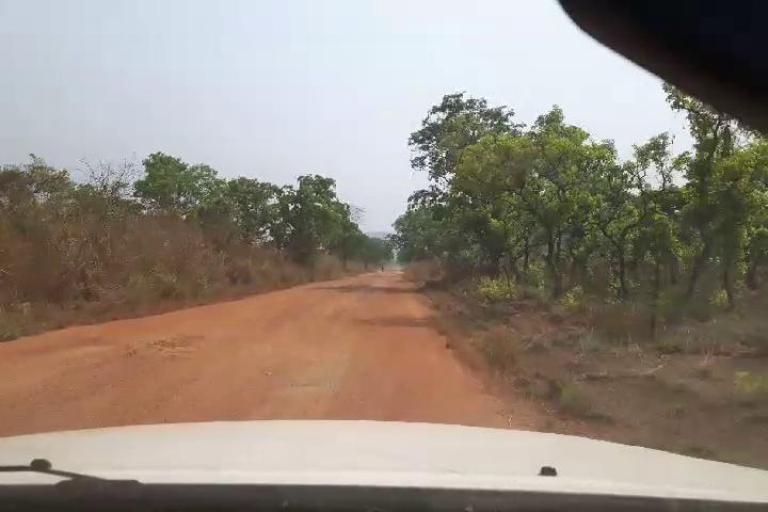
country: SL
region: Northern Province
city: Bumbuna
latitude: 8.9332
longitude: -11.8180
